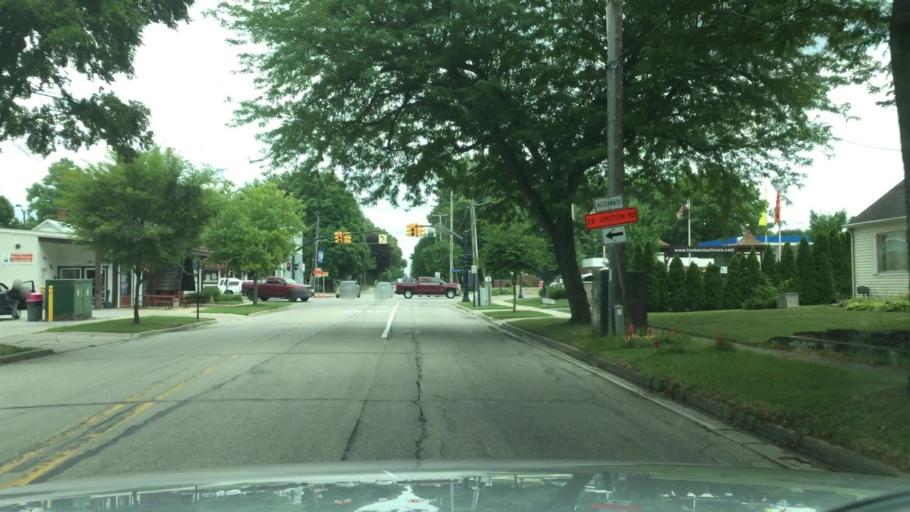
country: US
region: Michigan
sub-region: Saginaw County
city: Frankenmuth
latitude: 43.3217
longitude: -83.7415
